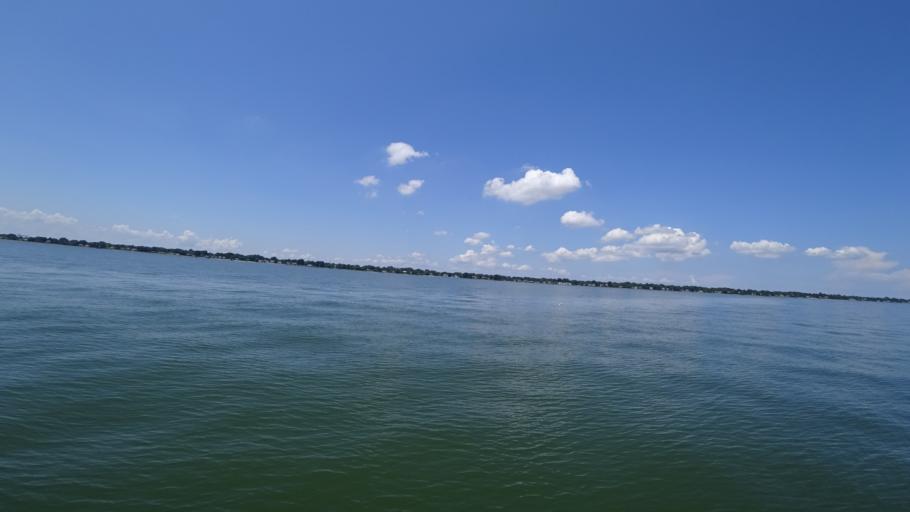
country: US
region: Virginia
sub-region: City of Hampton
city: Hampton
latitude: 36.9857
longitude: -76.3691
